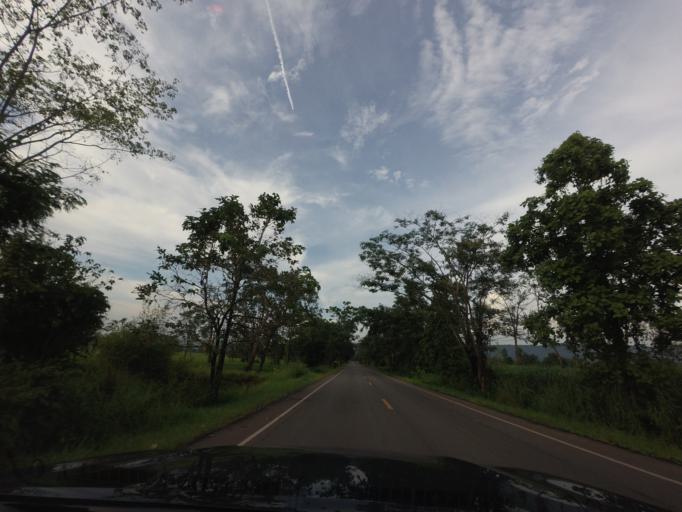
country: TH
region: Changwat Udon Thani
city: Nam Som
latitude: 17.8134
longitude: 102.2709
